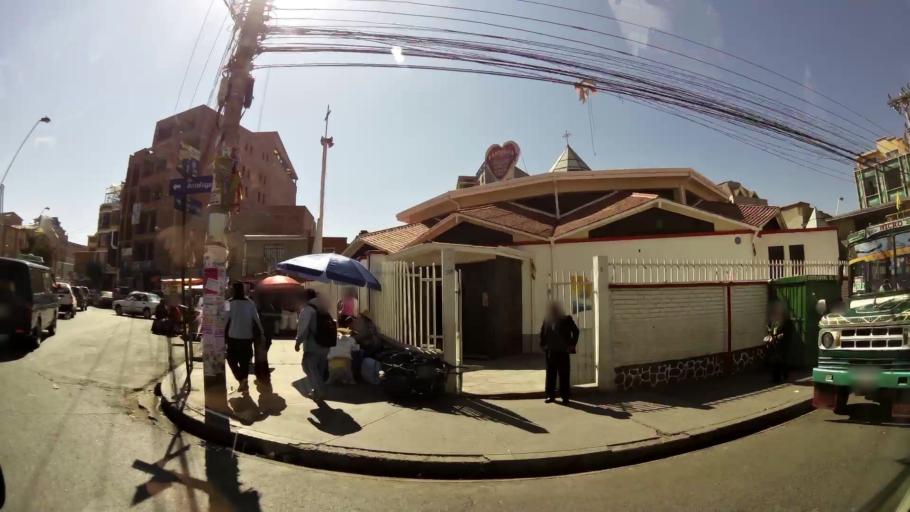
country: BO
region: La Paz
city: La Paz
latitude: -16.5101
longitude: -68.1587
